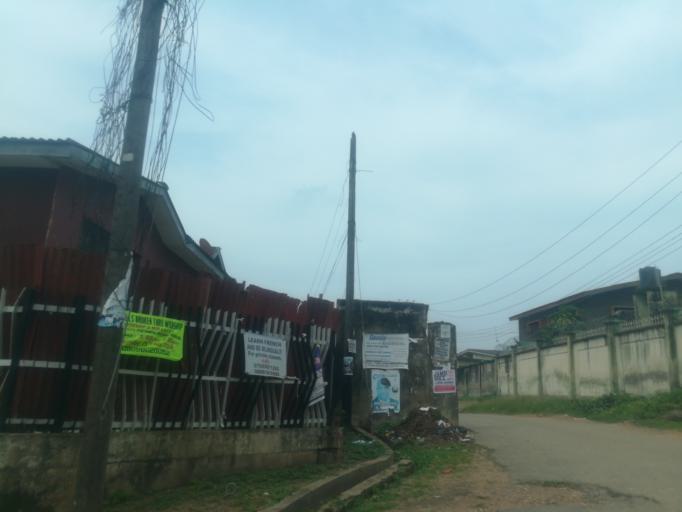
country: NG
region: Oyo
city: Ibadan
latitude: 7.4241
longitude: 3.9174
